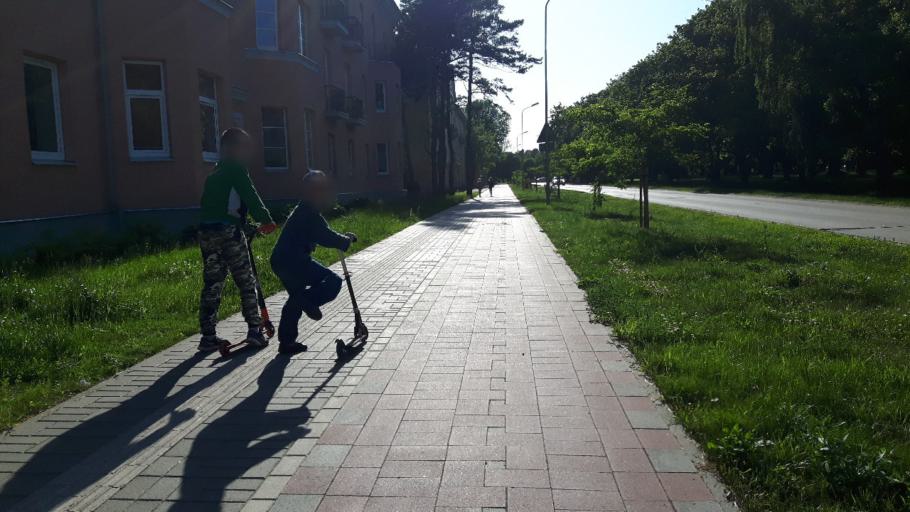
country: LV
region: Liepaja
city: Vec-Liepaja
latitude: 56.5483
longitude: 21.0103
